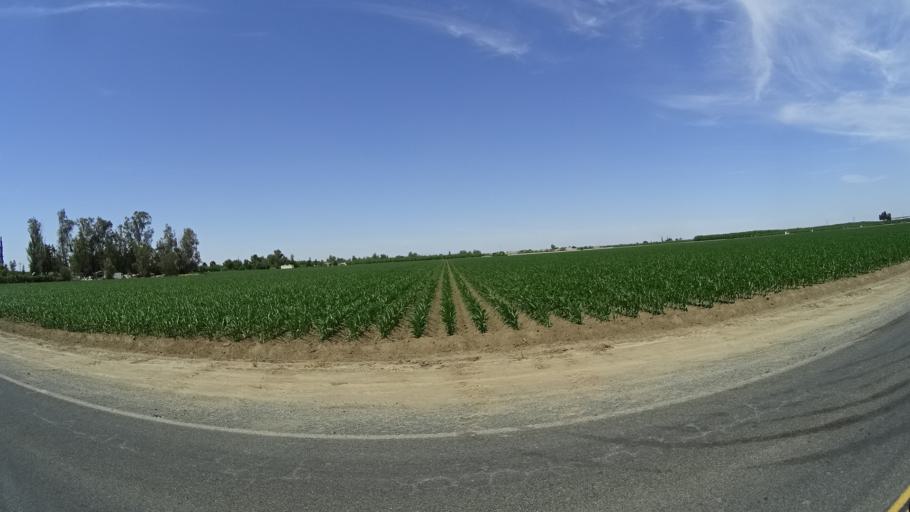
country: US
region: California
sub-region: Kings County
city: Armona
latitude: 36.3454
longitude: -119.6910
